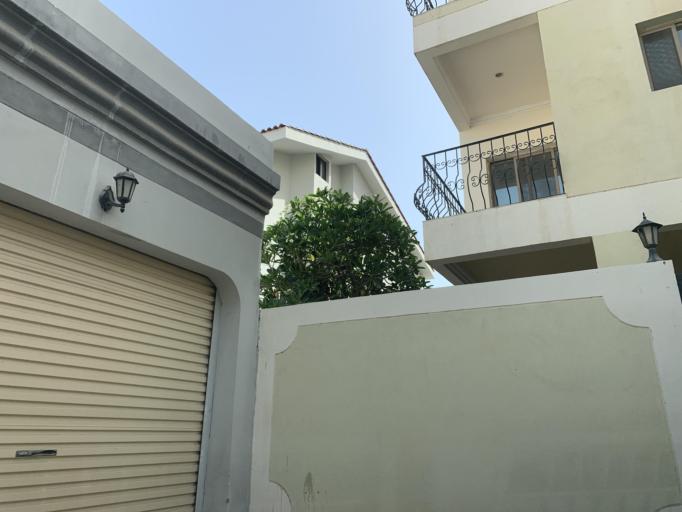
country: BH
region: Northern
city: Ar Rifa'
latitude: 26.1532
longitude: 50.5772
